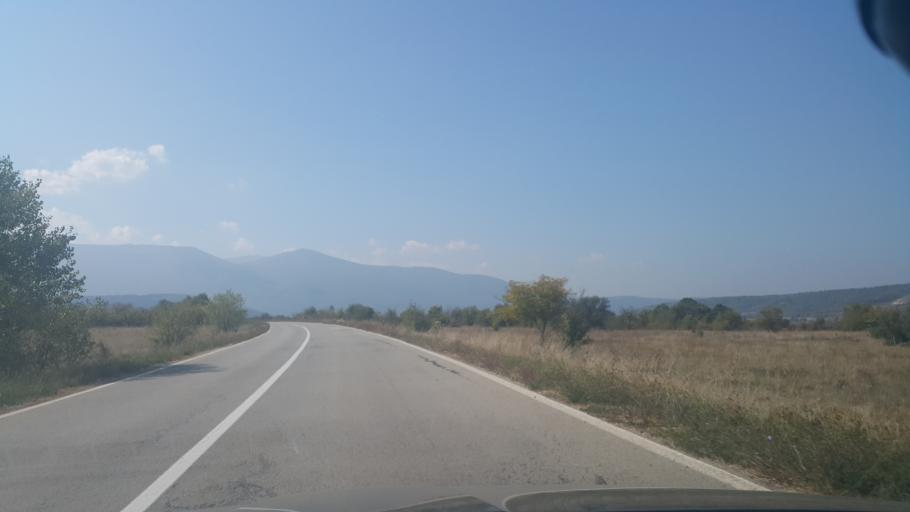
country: RS
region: Central Serbia
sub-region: Pirotski Okrug
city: Bela Palanka
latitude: 43.2271
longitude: 22.3740
